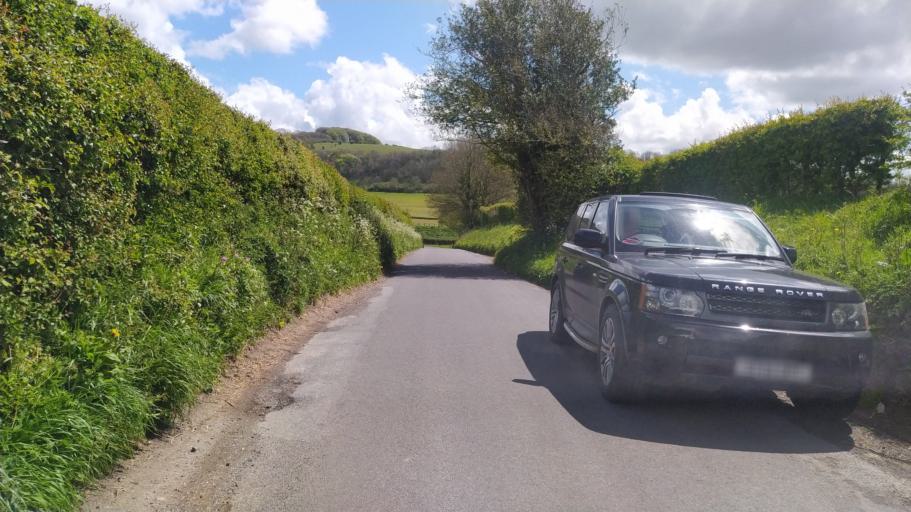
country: GB
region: England
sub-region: Wiltshire
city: Corsley
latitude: 51.1564
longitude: -2.2665
